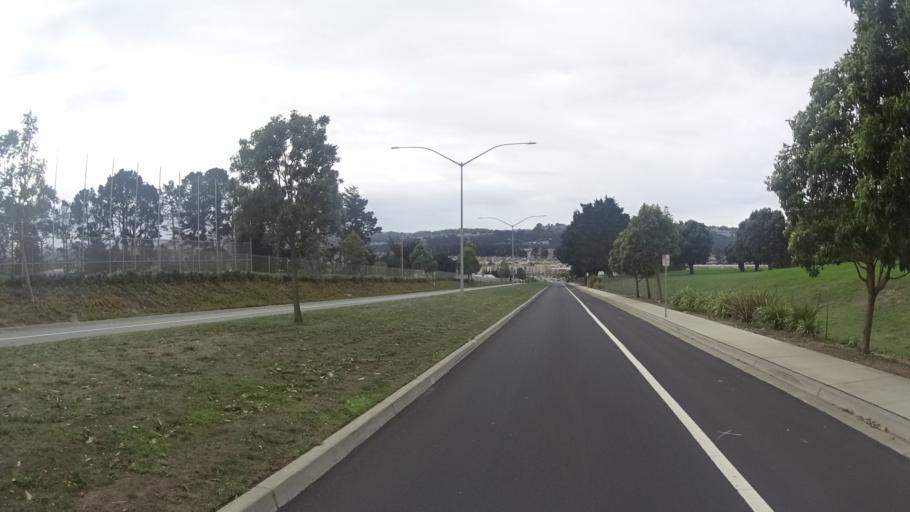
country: US
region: California
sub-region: San Mateo County
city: Colma
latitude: 37.6687
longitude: -122.4406
